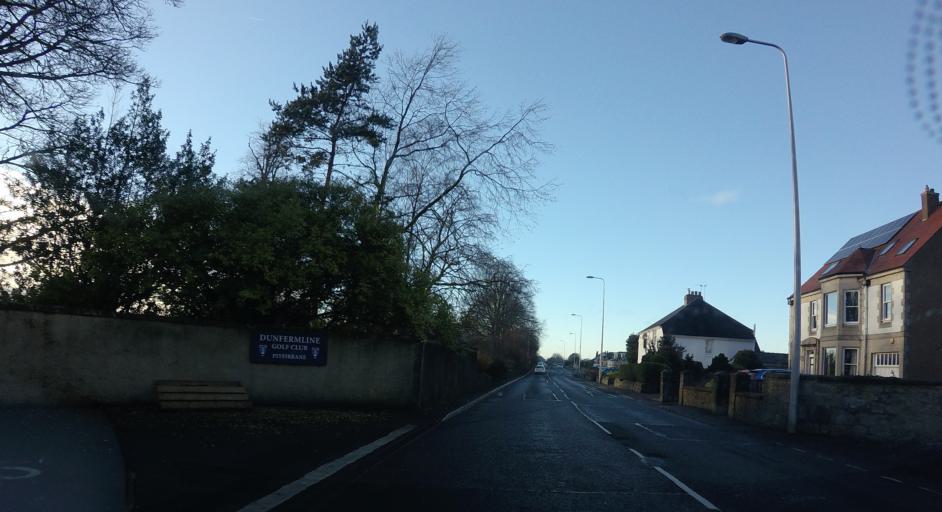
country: GB
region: Scotland
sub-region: Fife
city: Crossford
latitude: 56.0628
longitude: -3.5025
